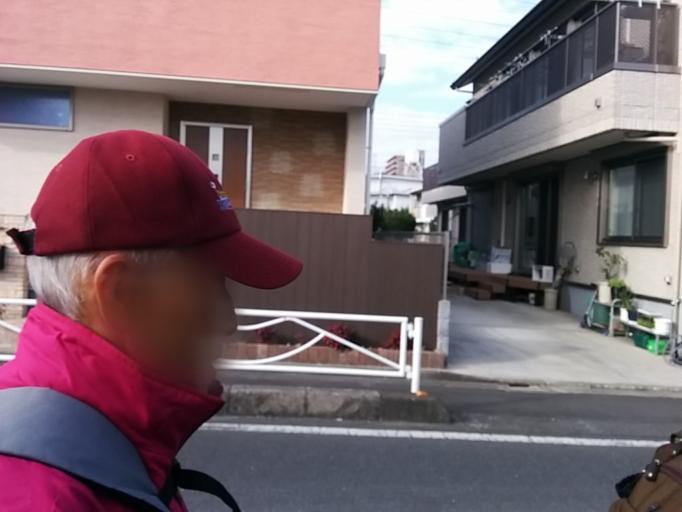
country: JP
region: Saitama
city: Kawagoe
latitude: 35.9064
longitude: 139.4897
